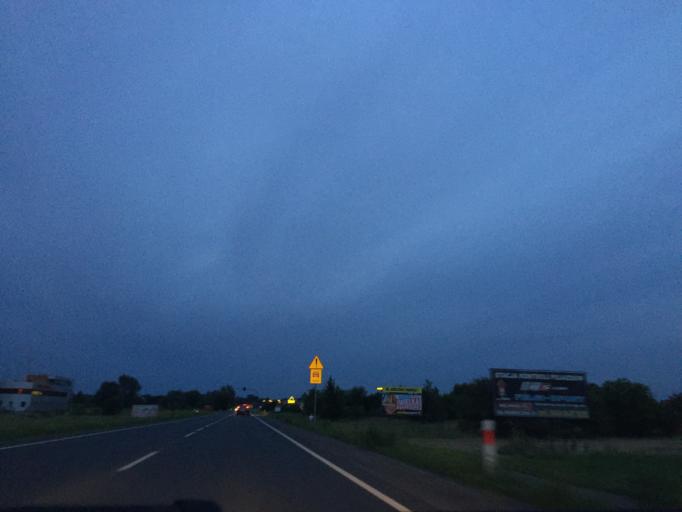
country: PL
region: Lesser Poland Voivodeship
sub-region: Powiat oswiecimski
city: Oswiecim
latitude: 50.0288
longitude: 19.2250
